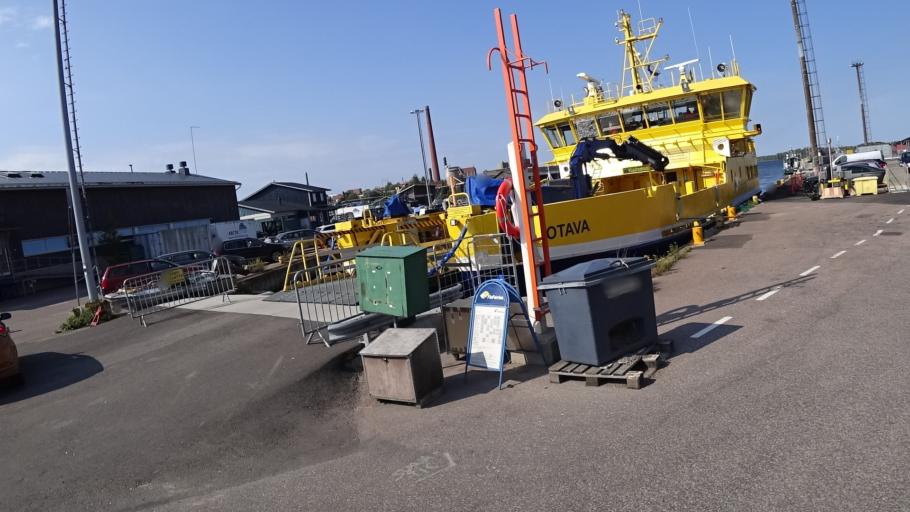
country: FI
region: Kymenlaakso
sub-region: Kotka-Hamina
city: Kotka
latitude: 60.4600
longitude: 26.9639
